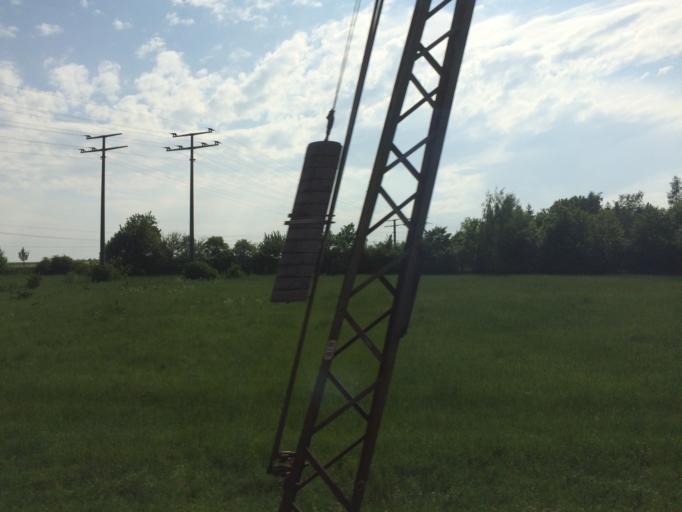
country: DE
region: Bavaria
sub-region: Regierungsbezirk Unterfranken
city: Iphofen
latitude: 49.6941
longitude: 10.2613
